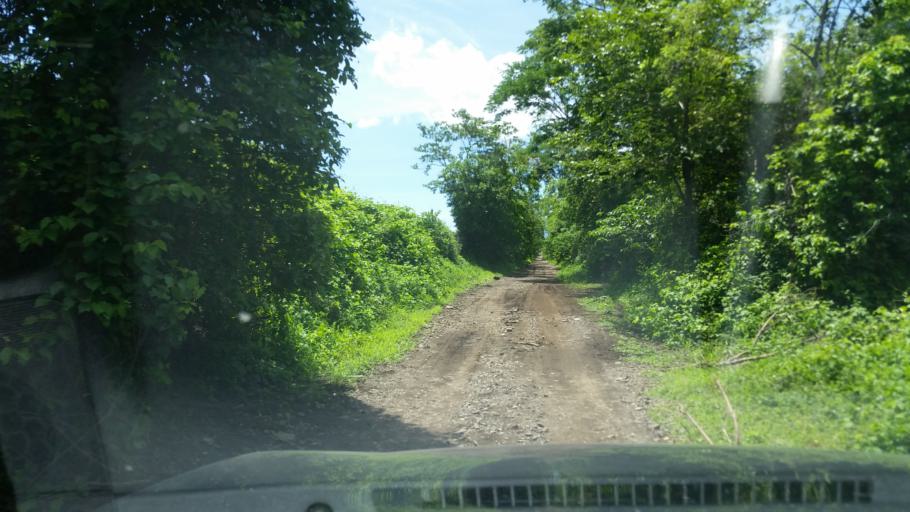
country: NI
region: Chinandega
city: Puerto Morazan
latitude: 12.7611
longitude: -87.1298
